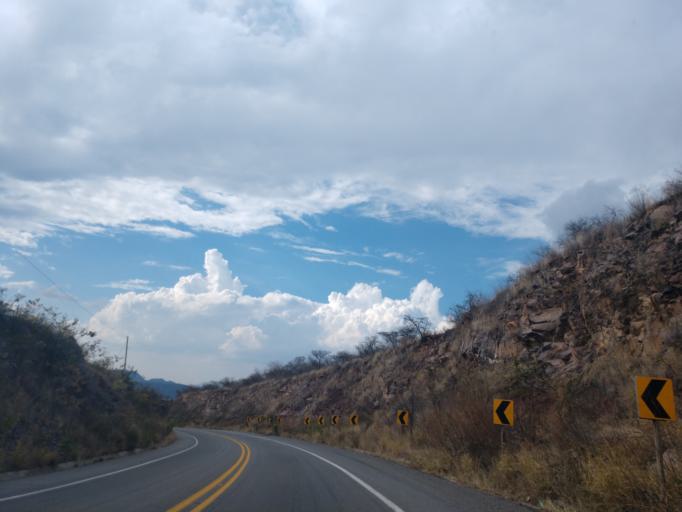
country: MX
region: Jalisco
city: La Manzanilla de la Paz
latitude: 20.0992
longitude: -103.1698
